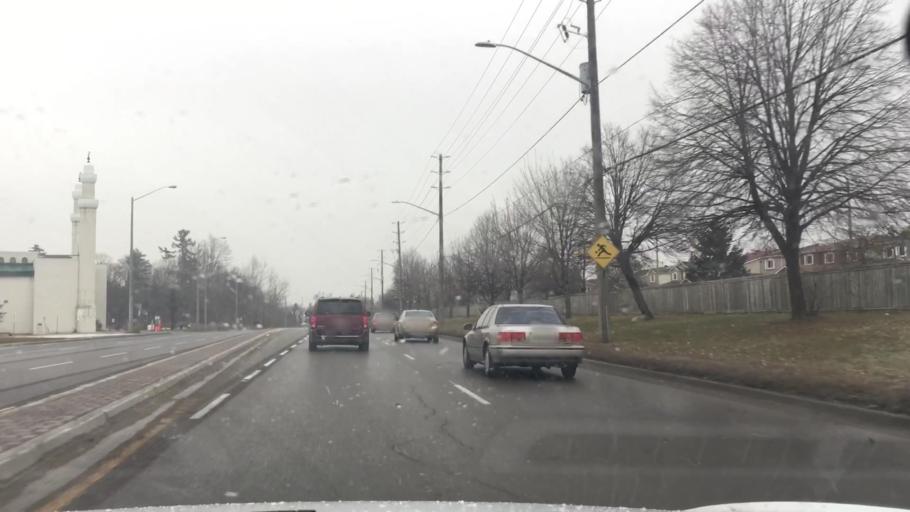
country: CA
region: Ontario
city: Ajax
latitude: 43.8543
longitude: -79.0774
